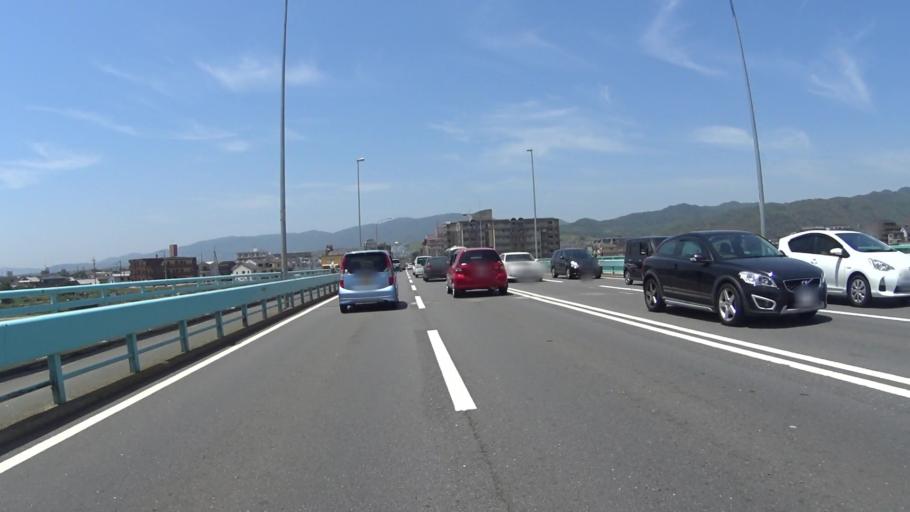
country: JP
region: Kyoto
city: Muko
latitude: 34.9943
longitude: 135.7104
